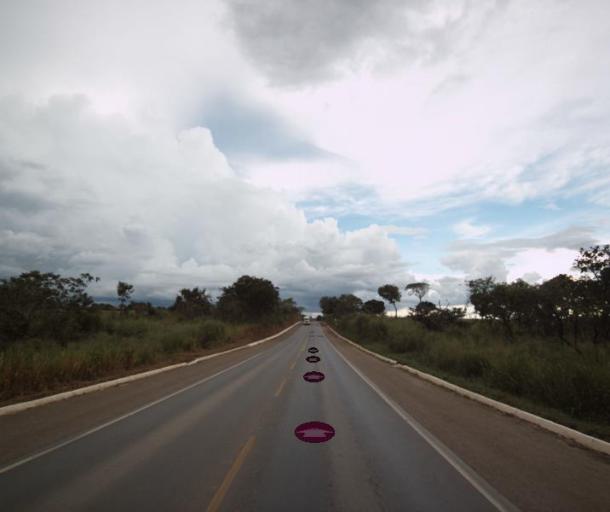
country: BR
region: Goias
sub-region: Itapaci
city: Itapaci
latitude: -14.8745
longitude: -49.3333
